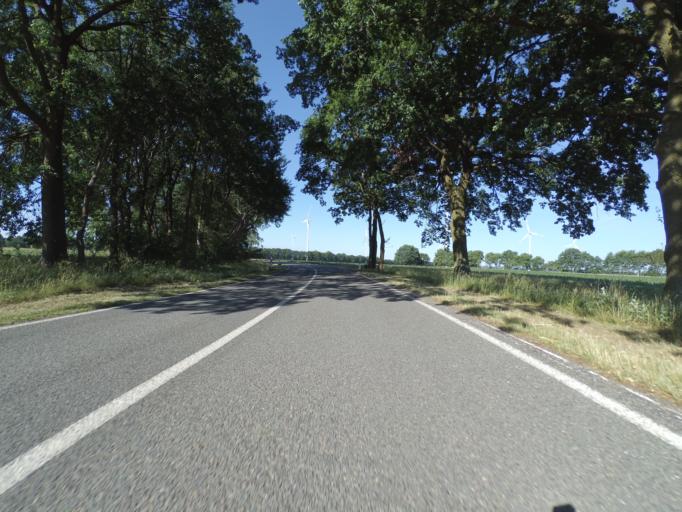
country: DE
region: Brandenburg
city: Putlitz
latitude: 53.3336
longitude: 12.0396
